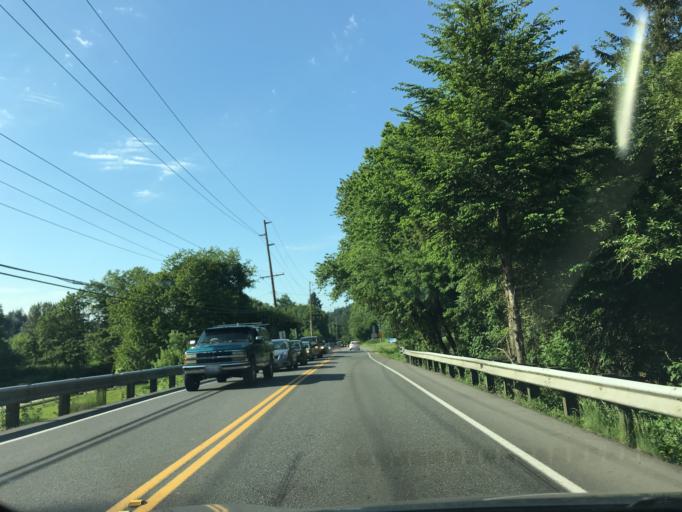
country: US
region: Washington
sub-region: King County
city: Issaquah
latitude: 47.5082
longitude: -122.0230
